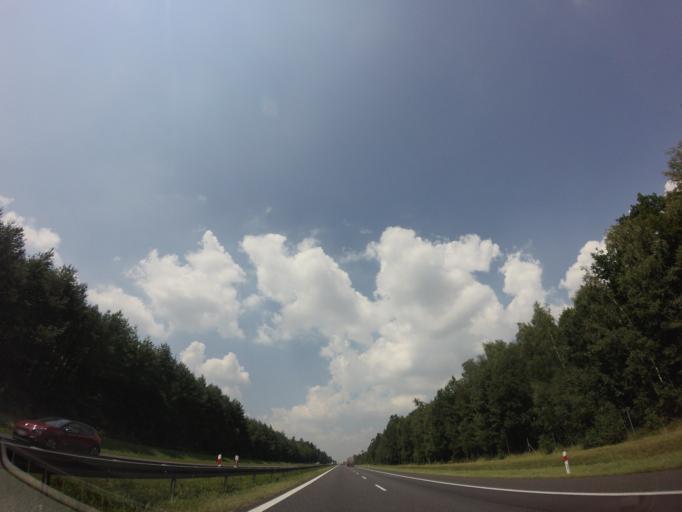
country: PL
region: Silesian Voivodeship
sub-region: Powiat gliwicki
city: Toszek
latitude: 50.3679
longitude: 18.5001
